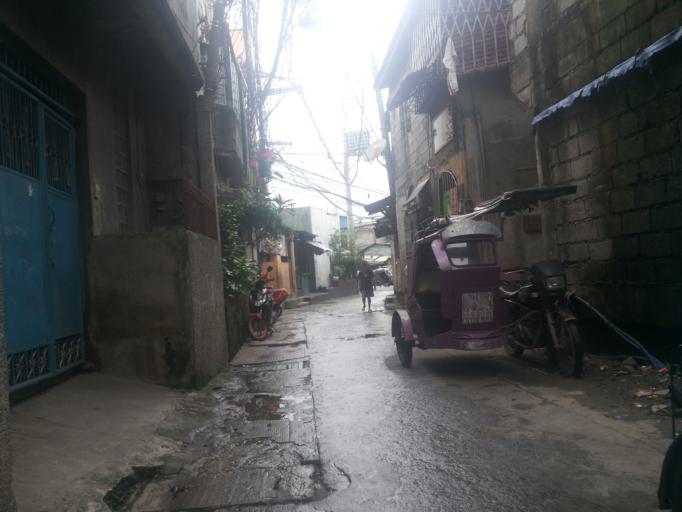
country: PH
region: Calabarzon
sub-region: Province of Rizal
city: Pateros
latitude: 14.5553
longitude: 121.0884
